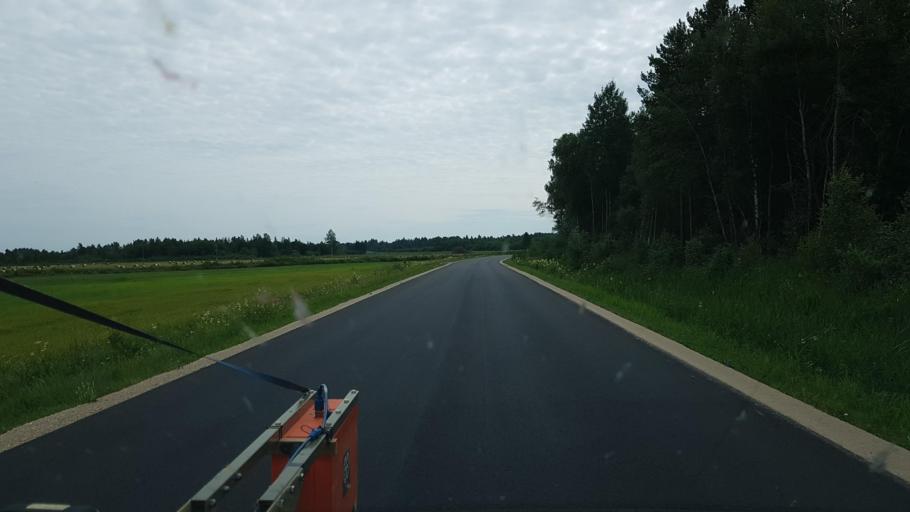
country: EE
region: Paernumaa
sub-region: Audru vald
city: Audru
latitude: 58.6220
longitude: 24.2684
